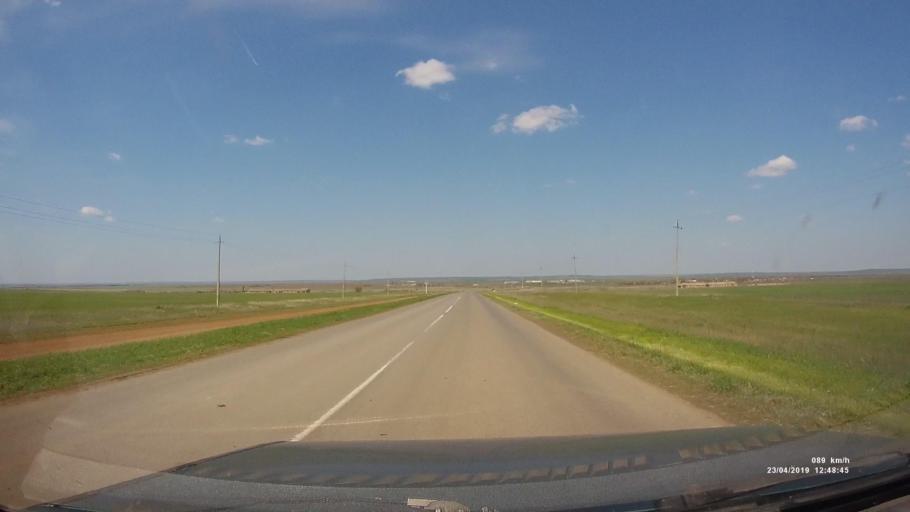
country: RU
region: Kalmykiya
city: Yashalta
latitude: 46.5284
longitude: 42.6389
